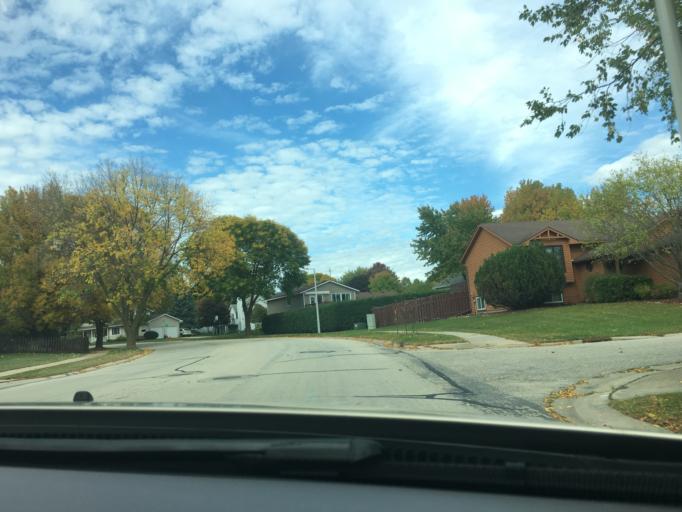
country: US
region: Minnesota
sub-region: Olmsted County
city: Rochester
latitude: 44.0815
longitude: -92.5217
